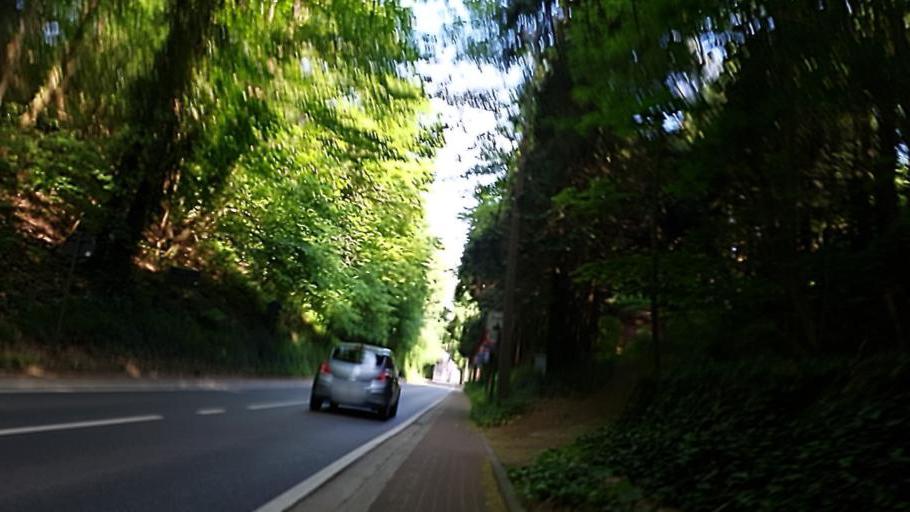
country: BE
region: Flanders
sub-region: Provincie Vlaams-Brabant
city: Overijse
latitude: 50.7700
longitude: 4.5453
